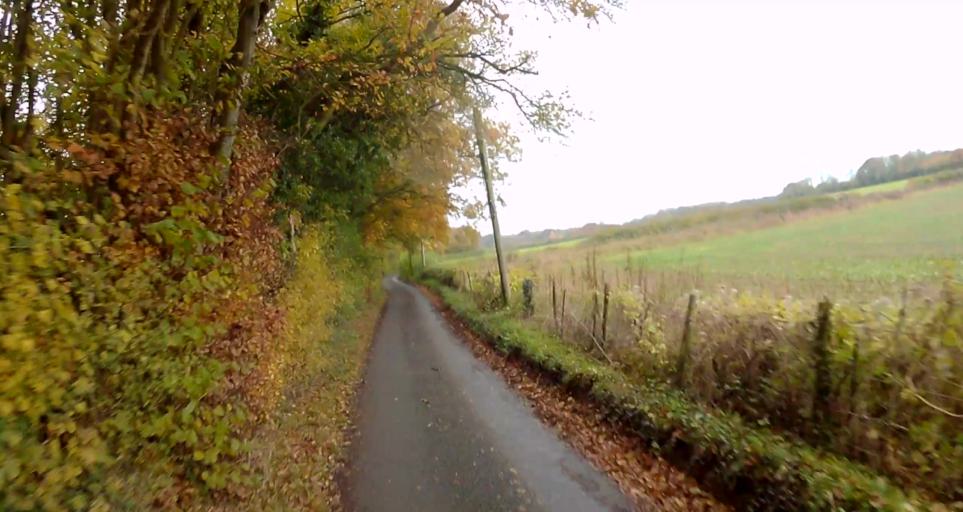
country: GB
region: England
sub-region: Hampshire
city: Long Sutton
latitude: 51.2372
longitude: -0.8925
